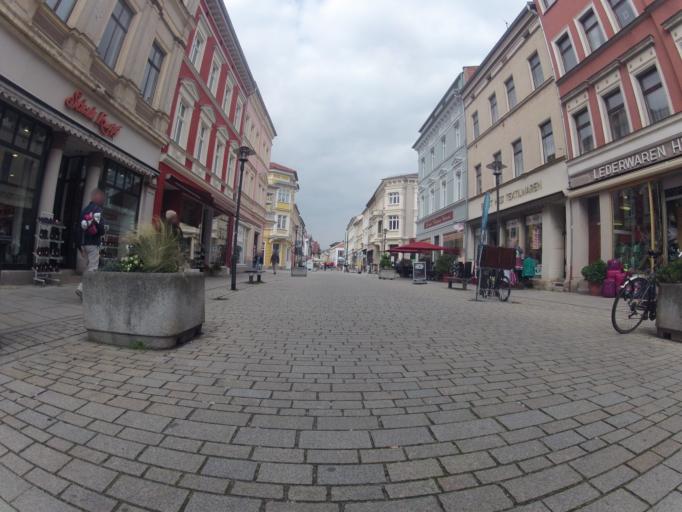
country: DE
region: Thuringia
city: Meiningen
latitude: 50.5684
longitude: 10.4154
